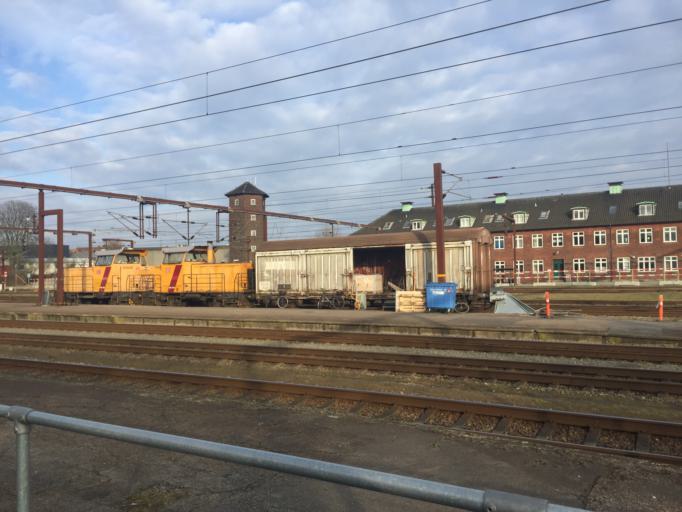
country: DK
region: South Denmark
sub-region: Fredericia Kommune
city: Fredericia
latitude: 55.5697
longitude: 9.7397
